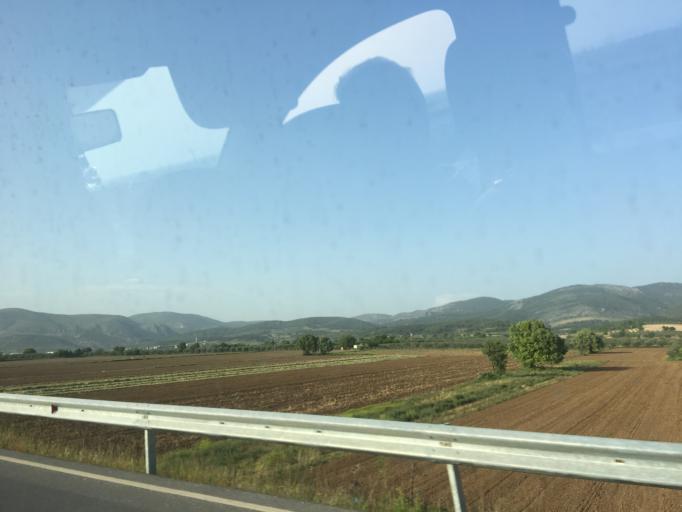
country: TR
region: Manisa
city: Golmarmara
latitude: 38.7953
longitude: 27.8975
